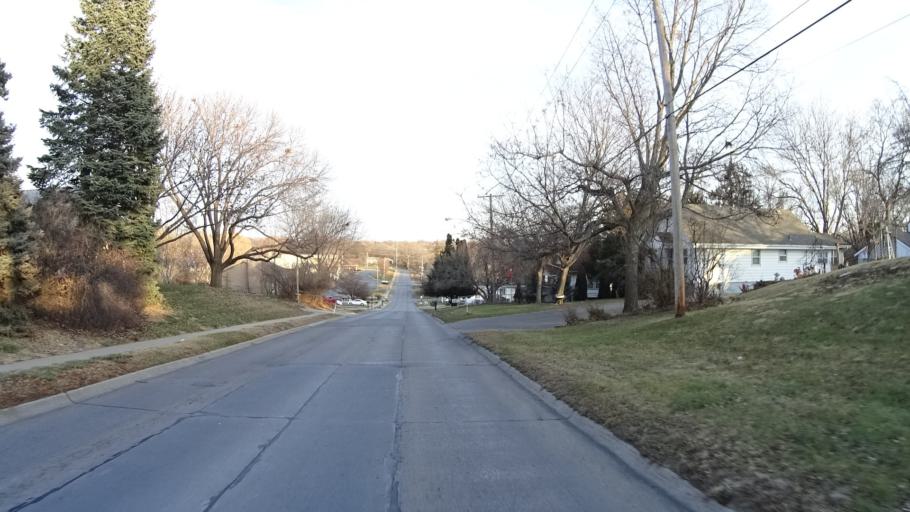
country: US
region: Nebraska
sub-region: Sarpy County
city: La Vista
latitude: 41.1764
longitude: -95.9719
